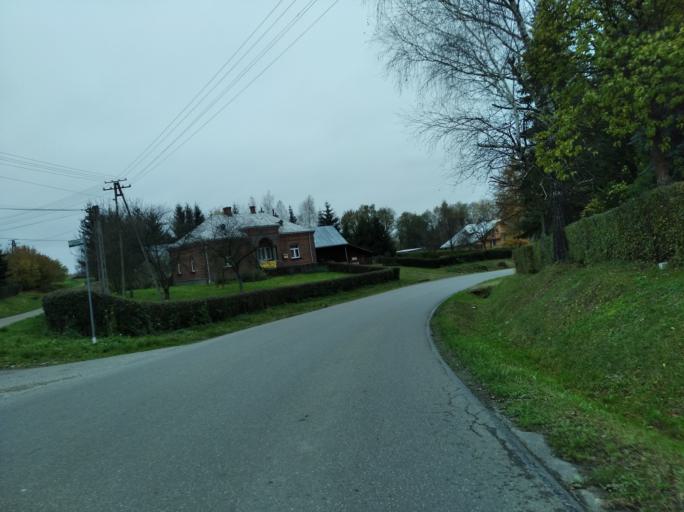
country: PL
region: Subcarpathian Voivodeship
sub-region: Powiat krosnienski
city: Chorkowka
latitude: 49.6739
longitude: 21.6821
